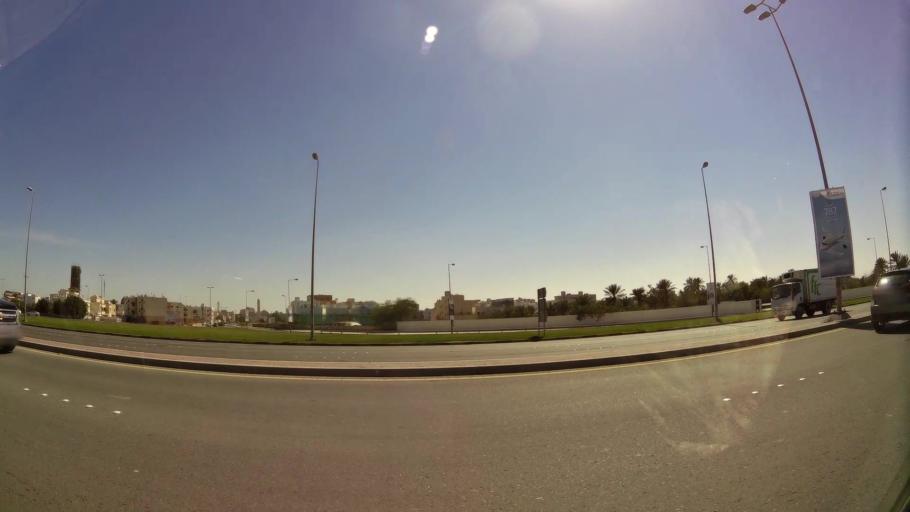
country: BH
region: Muharraq
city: Al Hadd
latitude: 26.2555
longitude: 50.6535
